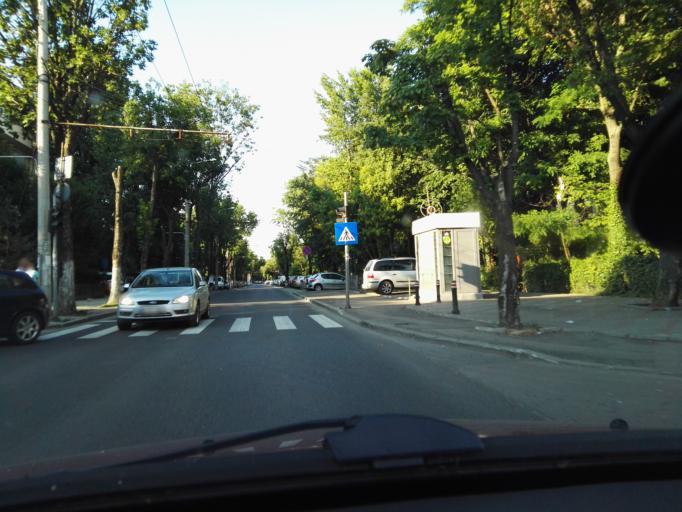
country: RO
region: Bucuresti
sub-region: Municipiul Bucuresti
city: Bucuresti
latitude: 44.3847
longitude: 26.1016
